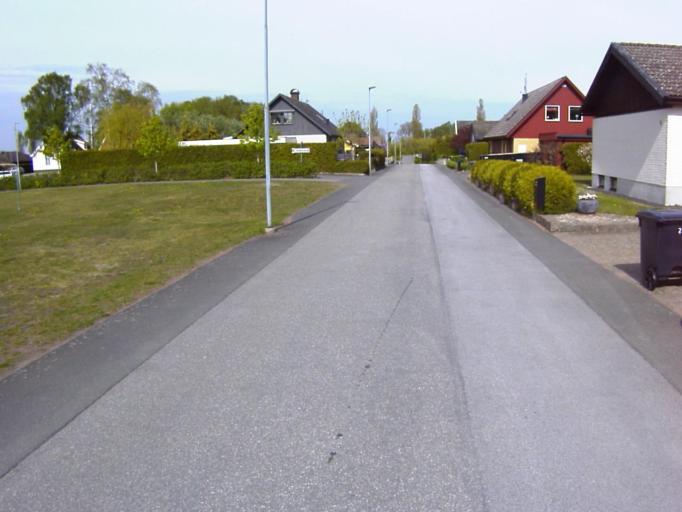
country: SE
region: Skane
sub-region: Kristianstads Kommun
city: Fjalkinge
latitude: 56.0386
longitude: 14.2771
